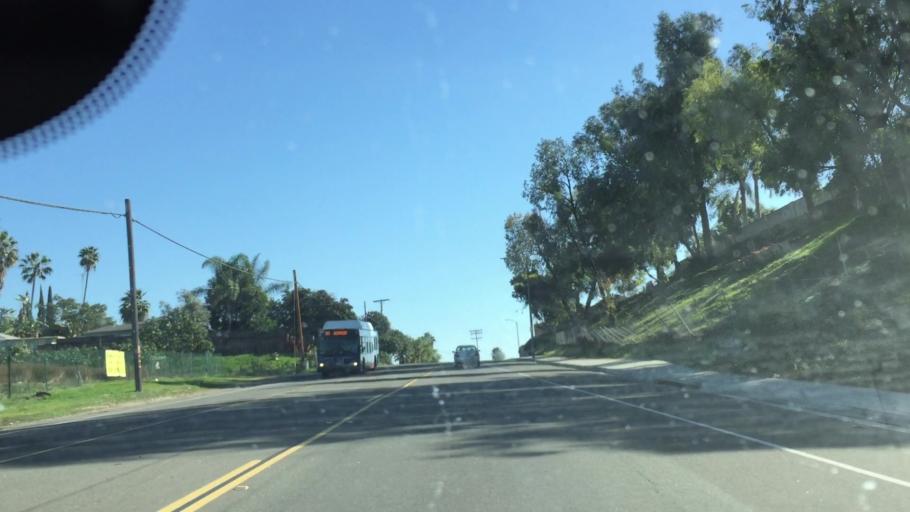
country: US
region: California
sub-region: San Diego County
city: Vista
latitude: 33.2277
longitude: -117.2472
